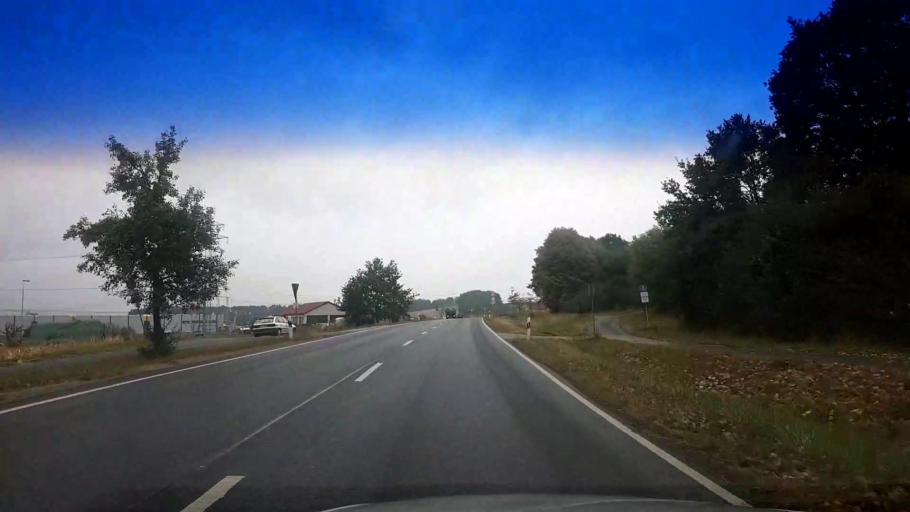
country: DE
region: Bavaria
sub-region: Upper Franconia
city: Forchheim
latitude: 49.7076
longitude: 11.0423
